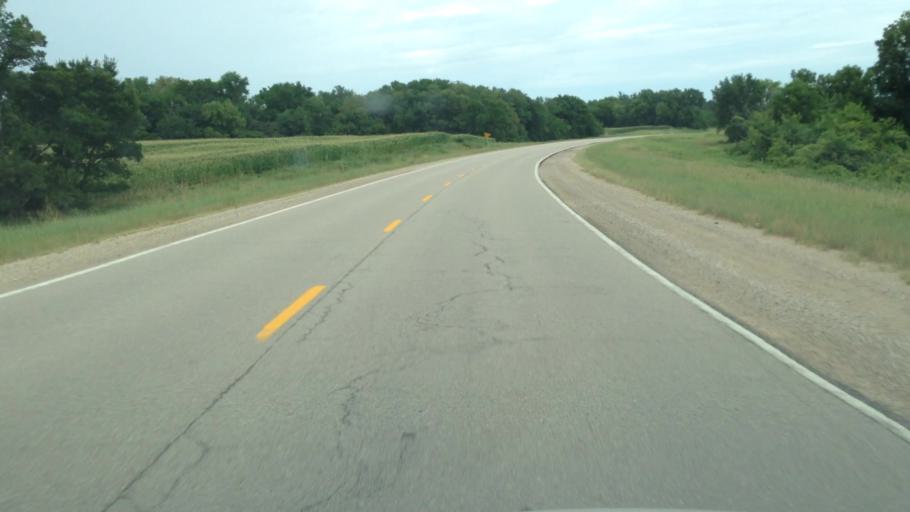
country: US
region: Kansas
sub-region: Jefferson County
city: Oskaloosa
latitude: 39.0939
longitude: -95.4767
